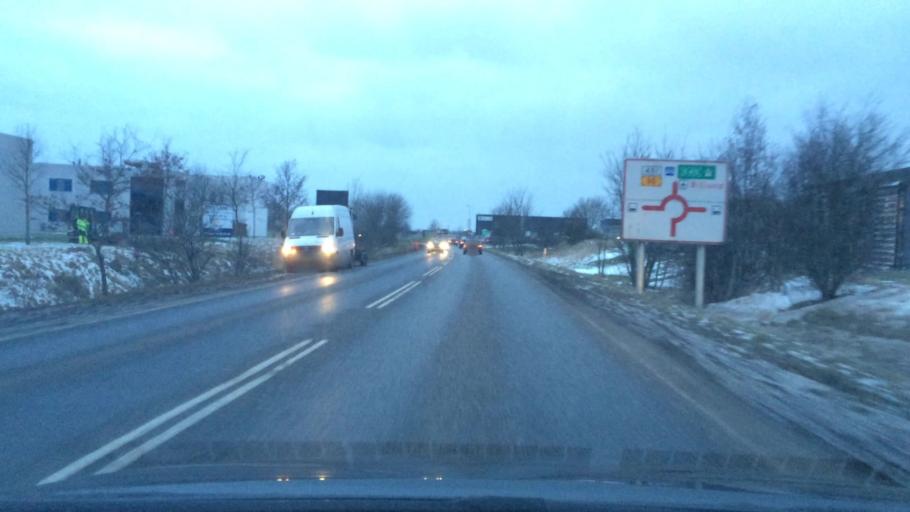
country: DK
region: Central Jutland
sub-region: Horsens Kommune
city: Horsens
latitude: 55.8331
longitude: 9.8016
